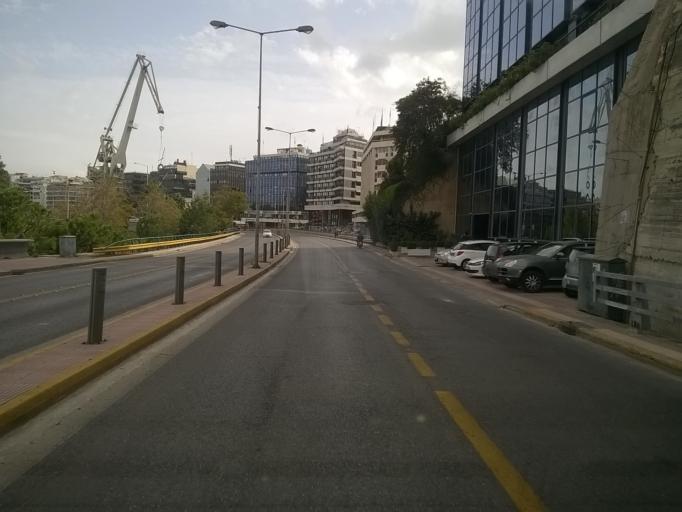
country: GR
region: Attica
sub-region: Nomos Attikis
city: Piraeus
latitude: 37.9374
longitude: 23.6348
